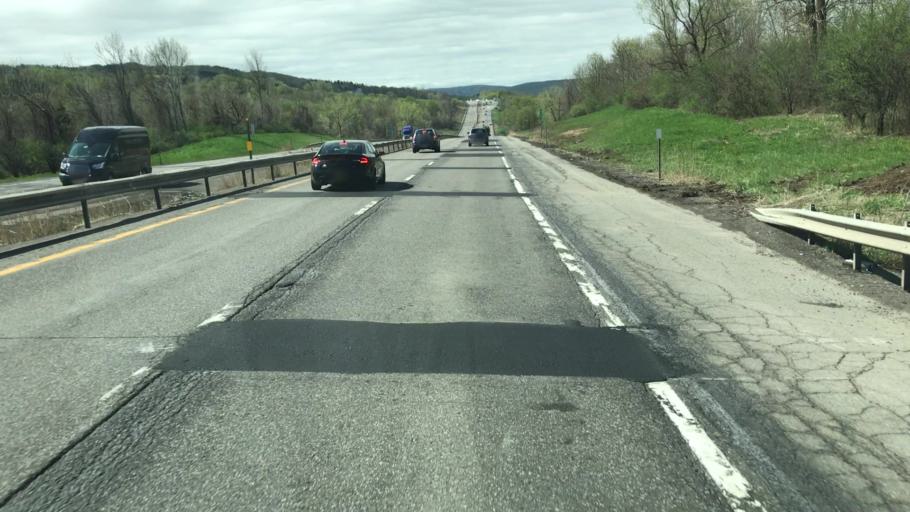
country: US
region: New York
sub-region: Onondaga County
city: Nedrow
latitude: 42.8722
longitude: -76.1112
